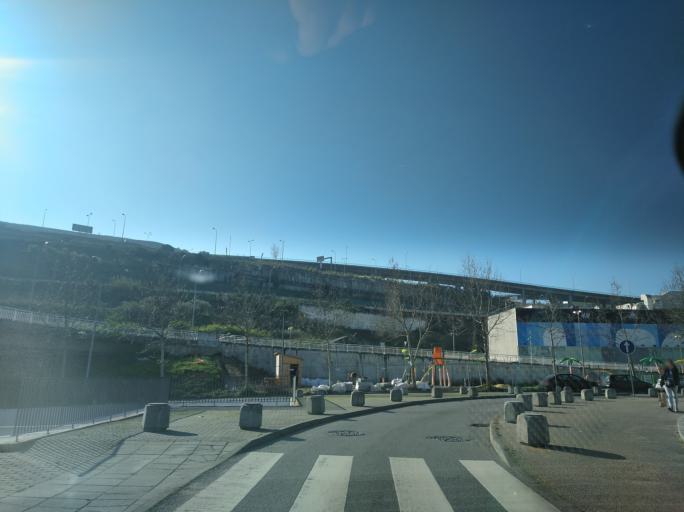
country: PT
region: Lisbon
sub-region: Odivelas
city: Famoes
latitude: 38.7749
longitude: -9.2198
